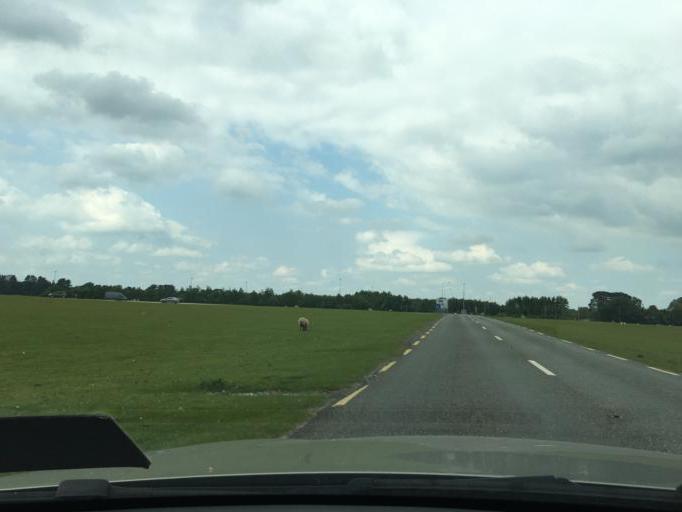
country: IE
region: Leinster
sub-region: Kildare
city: Athgarvan
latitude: 53.1583
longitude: -6.8263
